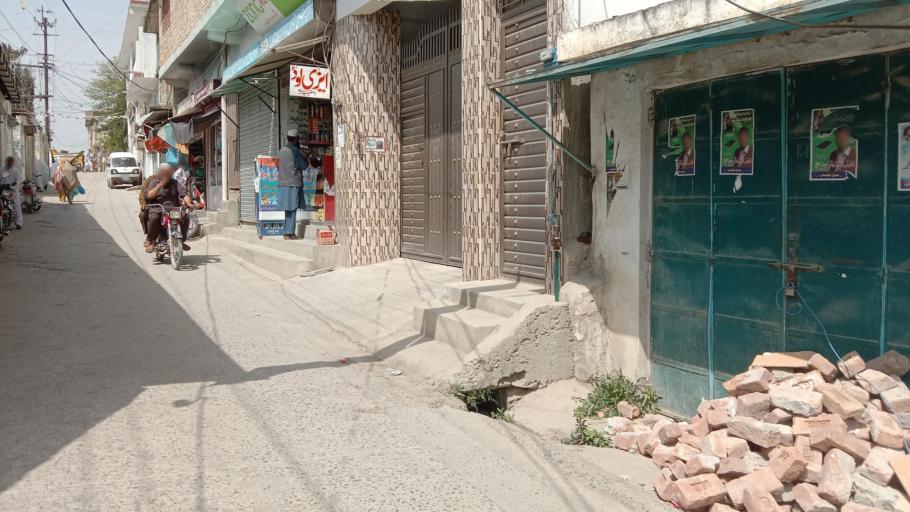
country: PK
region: Khyber Pakhtunkhwa
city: Abbottabad
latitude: 34.1652
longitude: 73.2626
